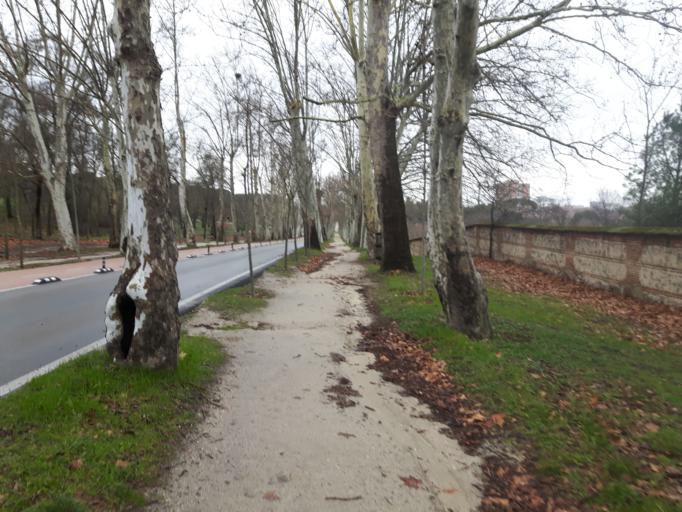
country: ES
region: Madrid
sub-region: Provincia de Madrid
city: Moncloa-Aravaca
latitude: 40.4211
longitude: -3.7300
